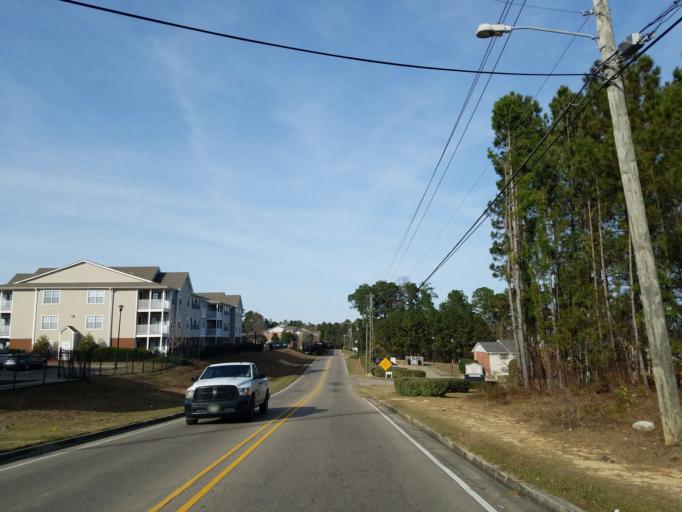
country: US
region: Mississippi
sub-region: Lamar County
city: Arnold Line
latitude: 31.3286
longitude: -89.3564
